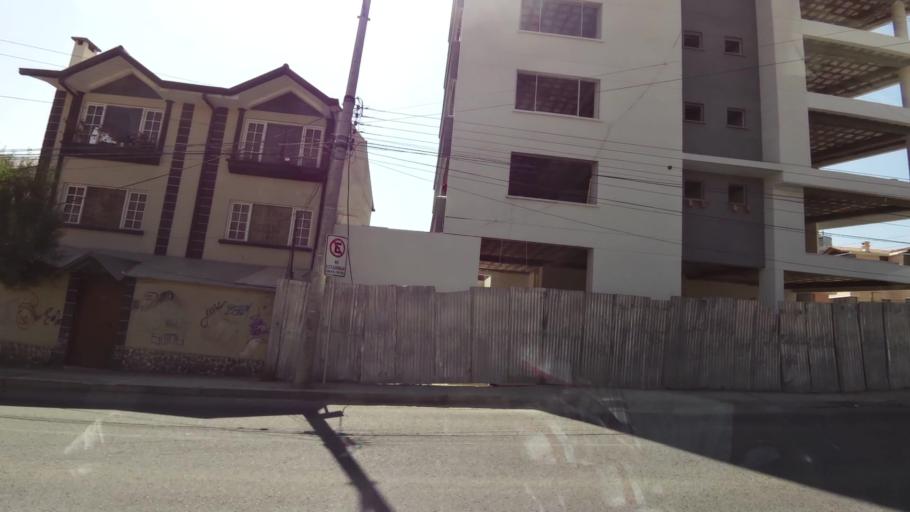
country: BO
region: La Paz
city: La Paz
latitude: -16.5464
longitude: -68.0782
